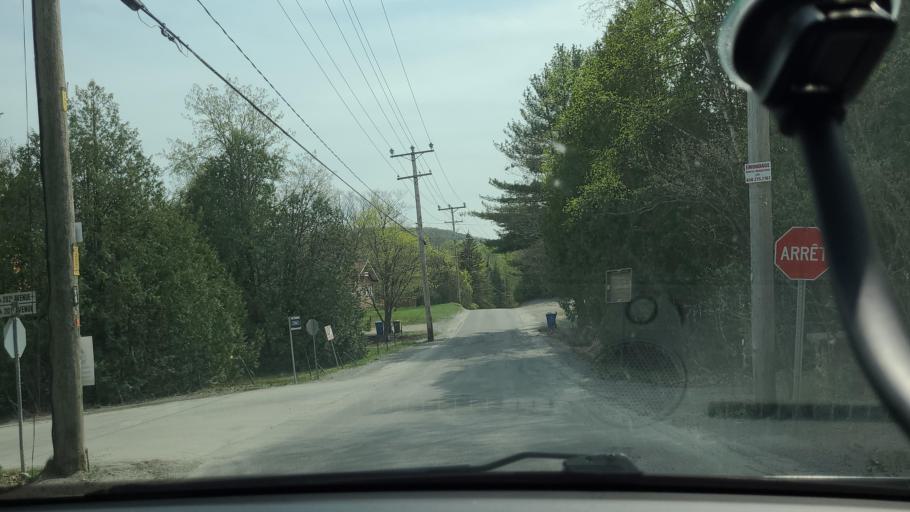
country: CA
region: Quebec
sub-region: Laurentides
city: Prevost
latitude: 45.8985
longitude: -74.0325
